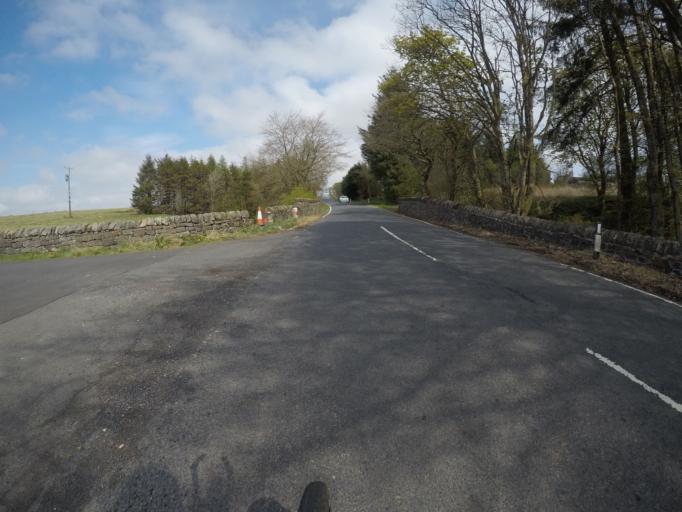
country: GB
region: Scotland
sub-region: East Renfrewshire
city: Neilston
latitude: 55.7194
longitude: -4.4334
